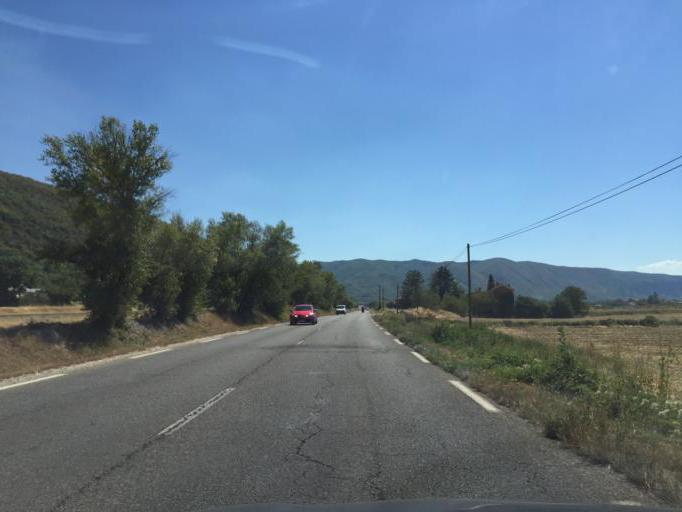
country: FR
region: Provence-Alpes-Cote d'Azur
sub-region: Departement des Alpes-de-Haute-Provence
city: Malijai
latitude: 44.0695
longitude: 6.0222
